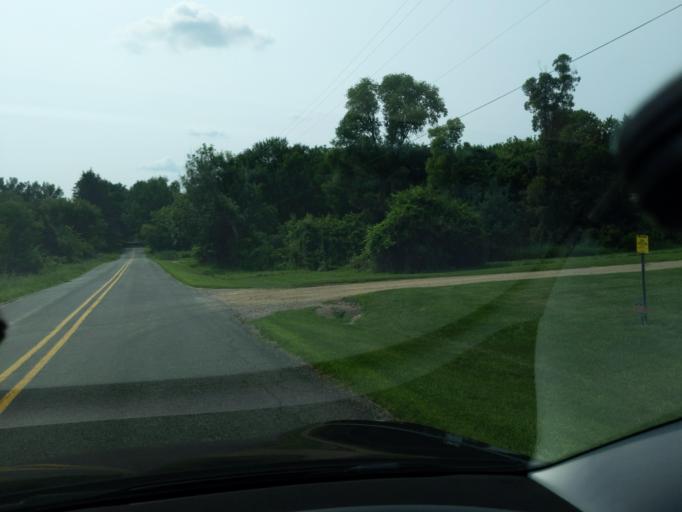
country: US
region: Michigan
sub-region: Ingham County
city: Holt
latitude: 42.6114
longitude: -84.5650
